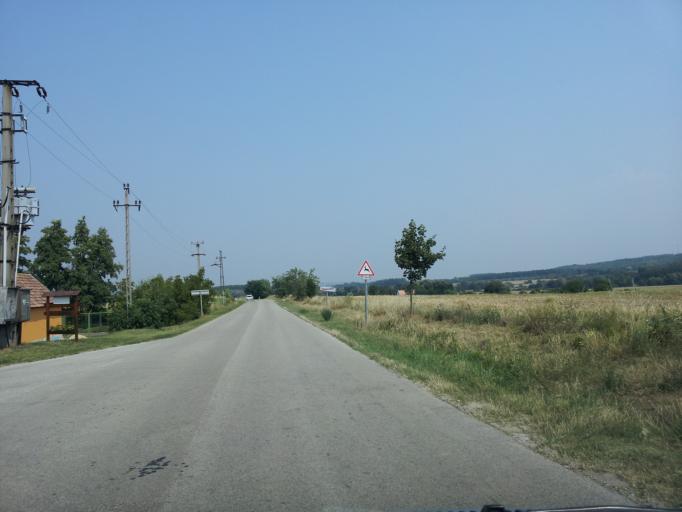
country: HU
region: Gyor-Moson-Sopron
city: Bakonyszentlaszlo
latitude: 47.3947
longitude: 17.8029
